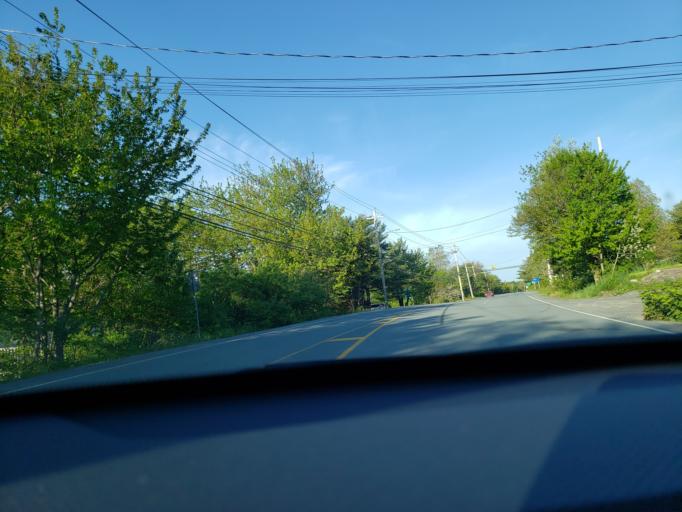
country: CA
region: Nova Scotia
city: Cole Harbour
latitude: 44.7226
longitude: -63.3987
